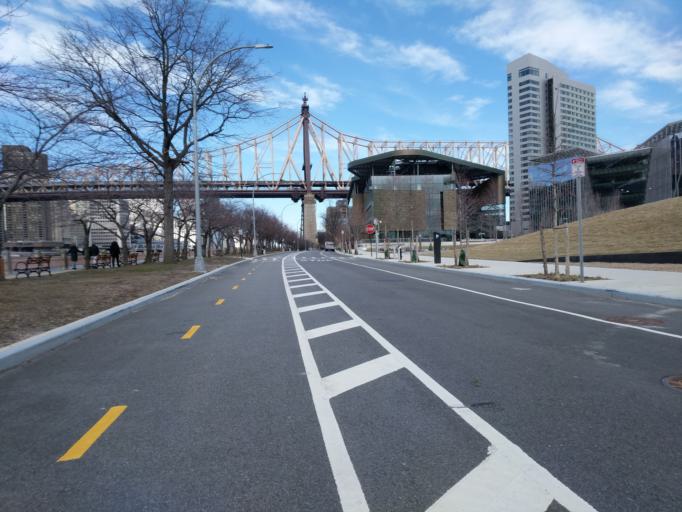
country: US
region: New York
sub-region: Queens County
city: Long Island City
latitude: 40.7545
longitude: -73.9578
